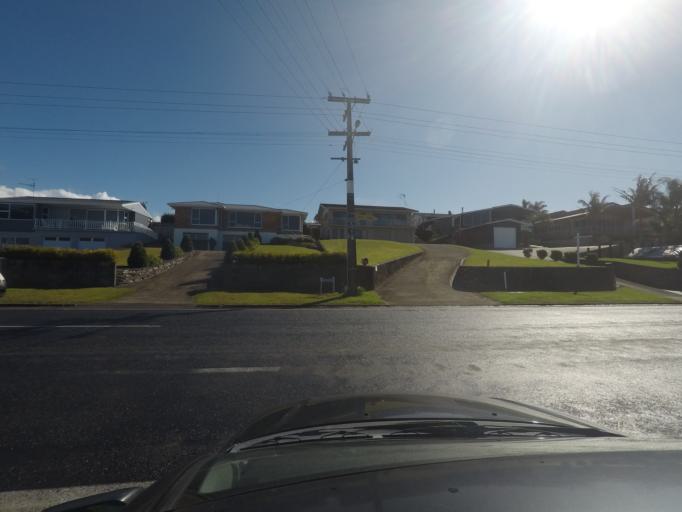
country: NZ
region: Bay of Plenty
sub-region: Western Bay of Plenty District
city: Waihi Beach
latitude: -37.4029
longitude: 175.9368
